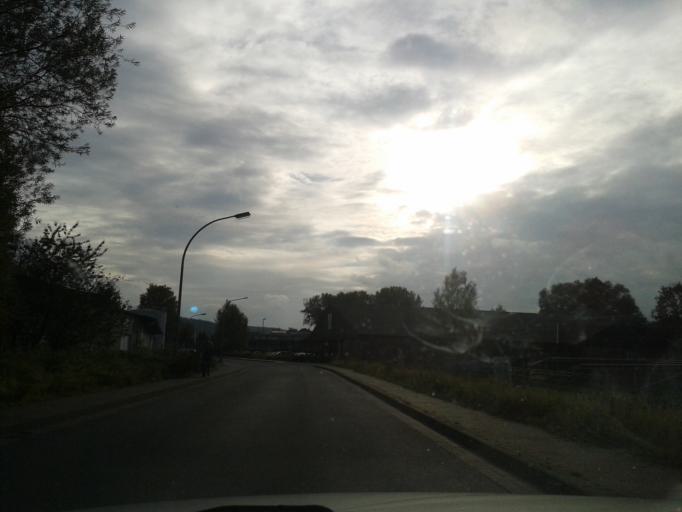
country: DE
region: North Rhine-Westphalia
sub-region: Regierungsbezirk Detmold
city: Horn-Bad Meinberg
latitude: 51.8811
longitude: 8.9535
